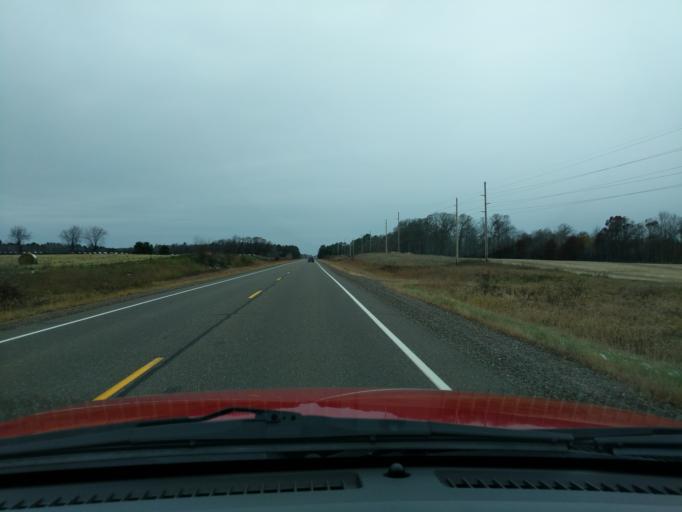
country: US
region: Wisconsin
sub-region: Washburn County
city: Shell Lake
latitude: 45.8155
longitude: -92.0801
